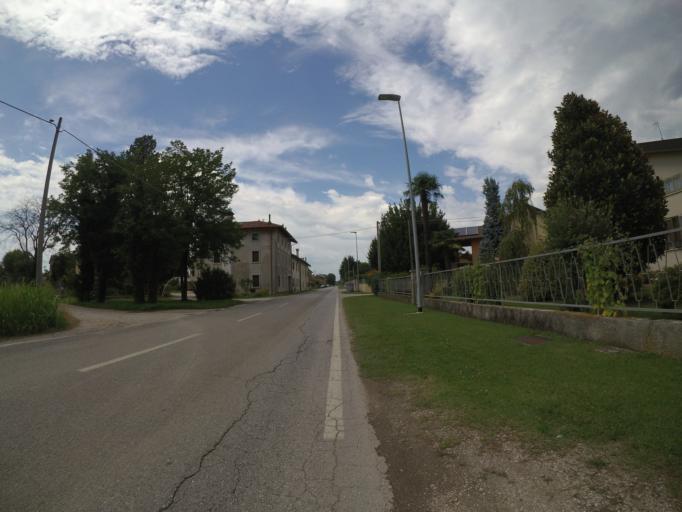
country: IT
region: Friuli Venezia Giulia
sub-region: Provincia di Udine
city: Talmassons
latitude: 45.9230
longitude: 13.1363
